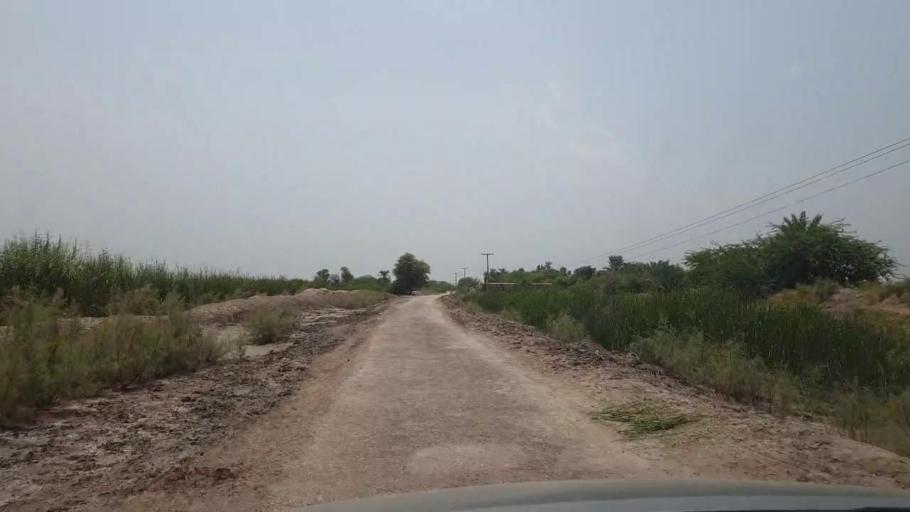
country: PK
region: Sindh
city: Garhi Yasin
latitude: 27.8801
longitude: 68.4952
